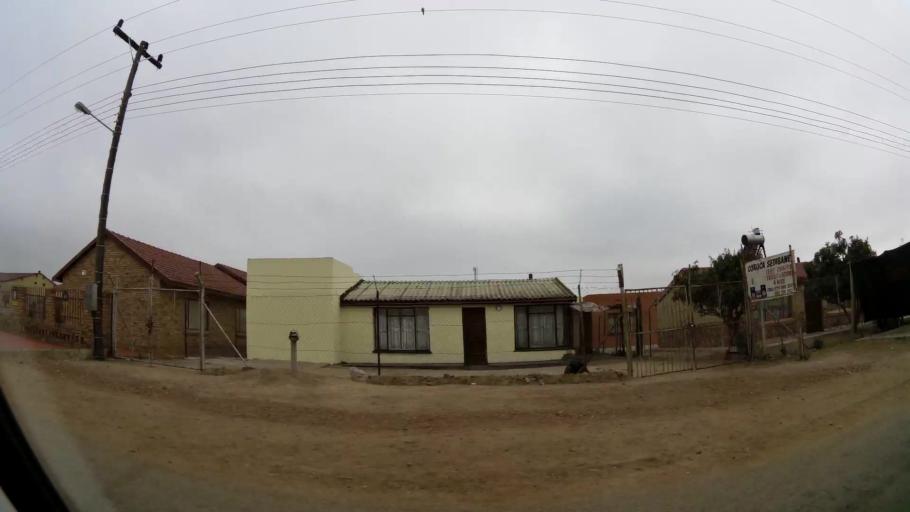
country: ZA
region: Limpopo
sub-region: Capricorn District Municipality
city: Polokwane
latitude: -23.8411
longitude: 29.3902
